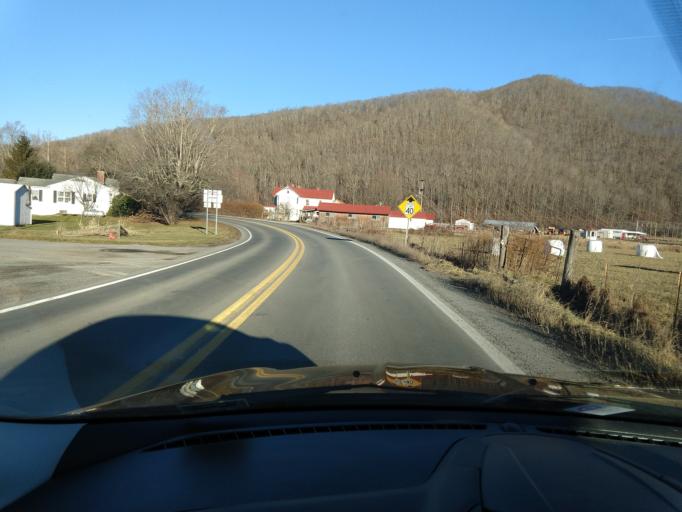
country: US
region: Virginia
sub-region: Highland County
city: Monterey
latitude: 38.5415
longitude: -79.7835
